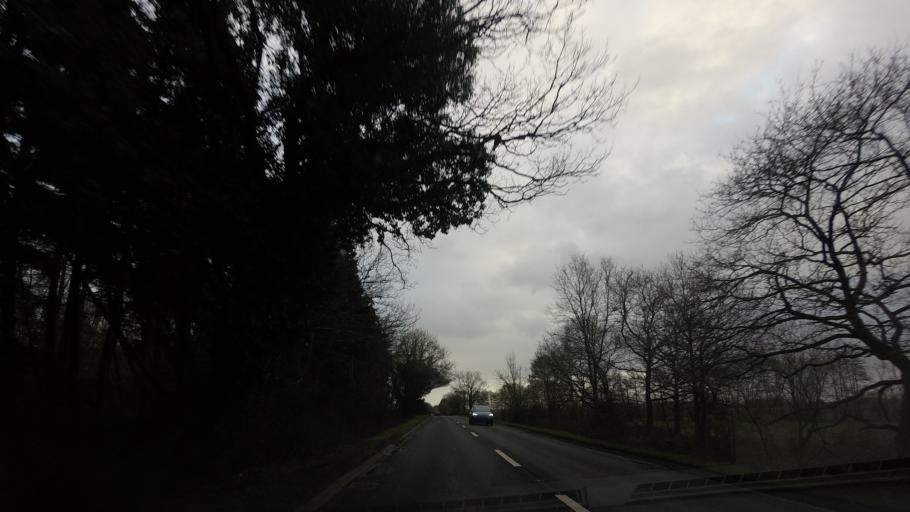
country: GB
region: England
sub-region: Kent
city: East Peckham
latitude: 51.2310
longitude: 0.3861
